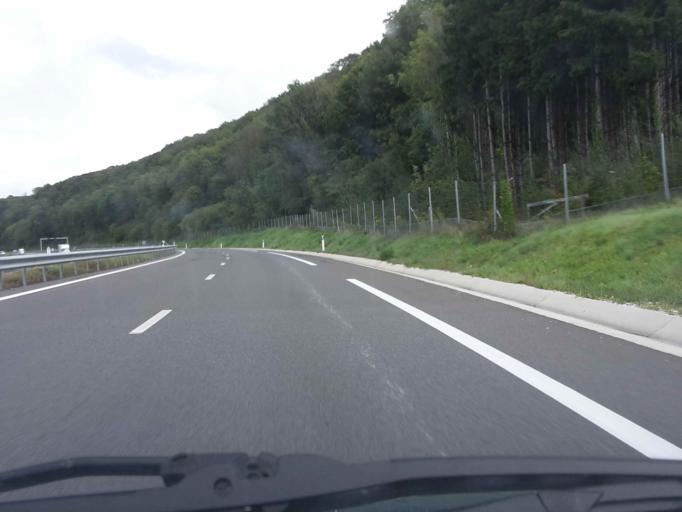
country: FR
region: Franche-Comte
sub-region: Departement du Doubs
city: Morre
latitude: 47.2088
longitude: 6.0429
